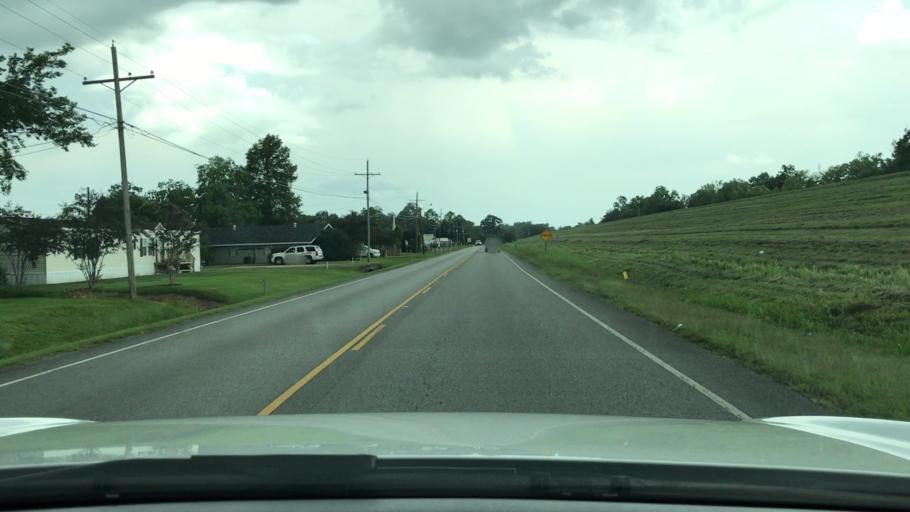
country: US
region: Louisiana
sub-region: Iberville Parish
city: Plaquemine
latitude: 30.2788
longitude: -91.2181
